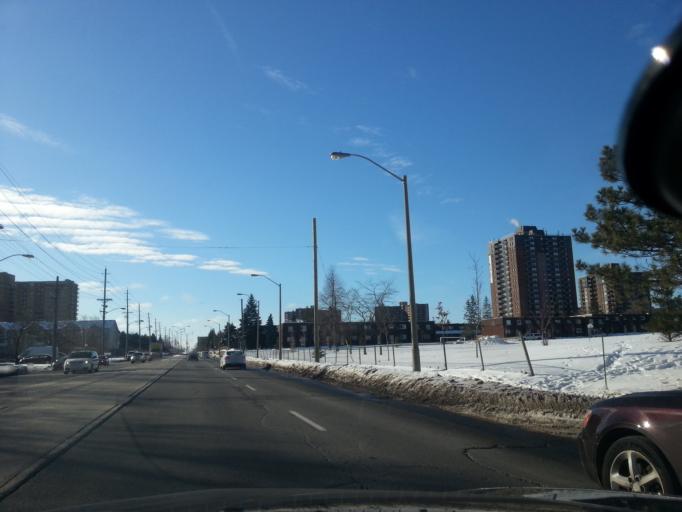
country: CA
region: Ontario
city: Ottawa
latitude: 45.3775
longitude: -75.6461
